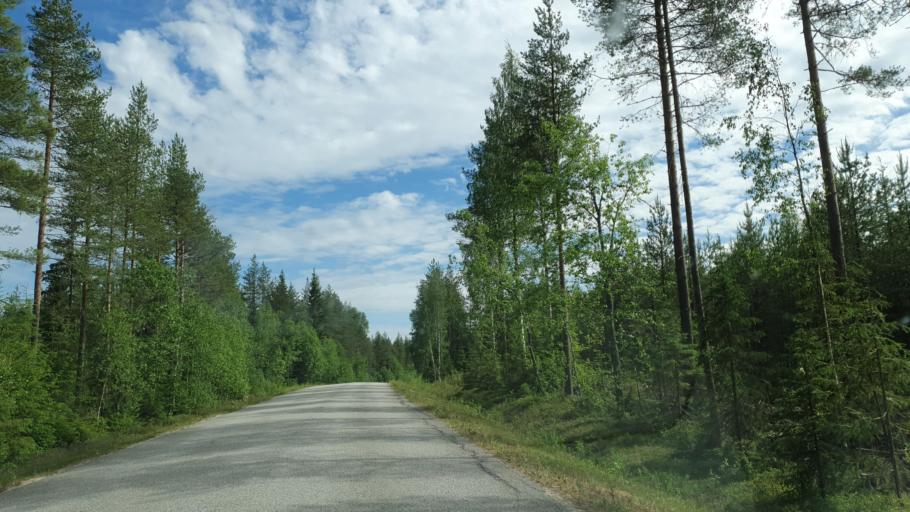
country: FI
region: Kainuu
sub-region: Kehys-Kainuu
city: Suomussalmi
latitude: 64.5831
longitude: 29.1213
